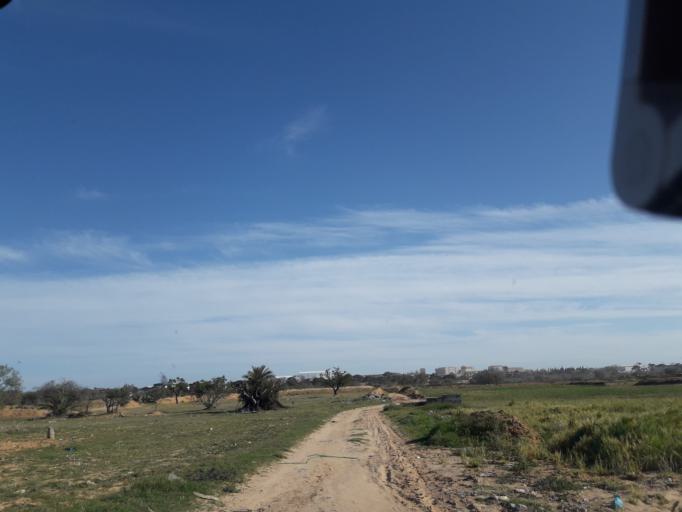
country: TN
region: Safaqis
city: Sfax
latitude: 34.7365
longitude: 10.5175
